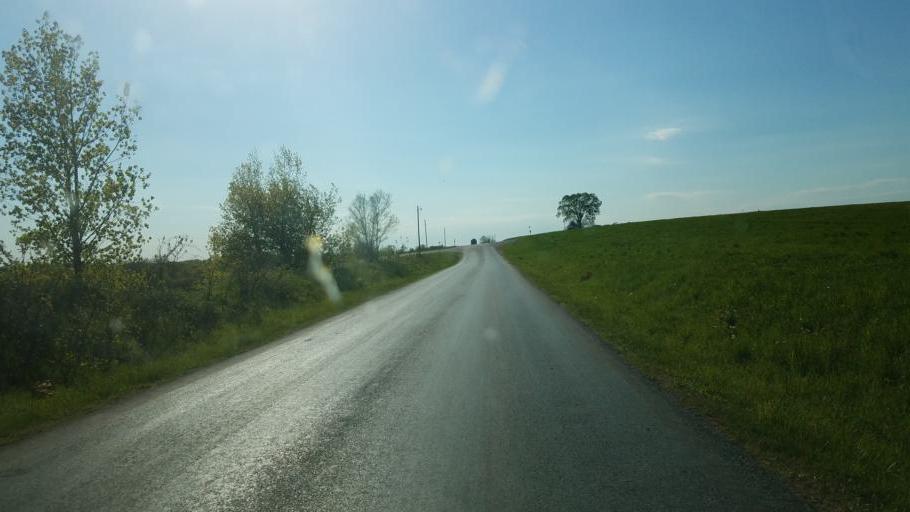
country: US
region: Wisconsin
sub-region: Vernon County
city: Hillsboro
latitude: 43.6846
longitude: -90.3800
